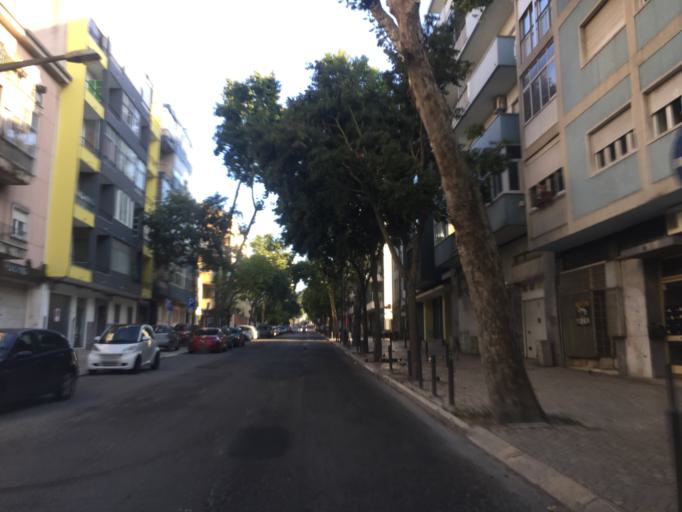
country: PT
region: Lisbon
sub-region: Odivelas
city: Pontinha
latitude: 38.7478
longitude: -9.1978
